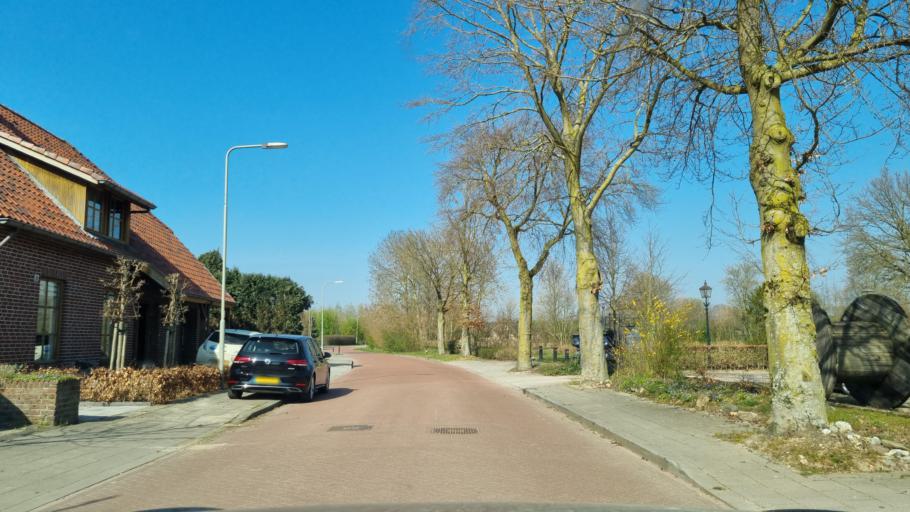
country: NL
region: Limburg
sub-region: Gemeente Gennep
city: Gennep
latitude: 51.7165
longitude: 6.0255
